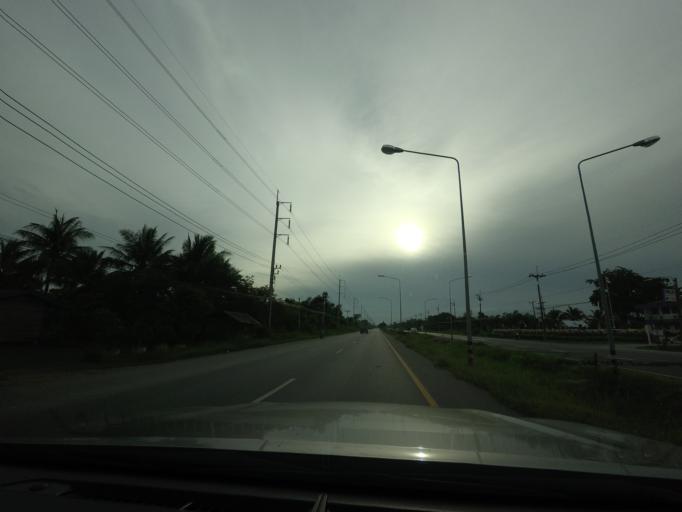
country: TH
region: Nakhon Si Thammarat
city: Hua Sai
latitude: 8.0477
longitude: 100.2720
